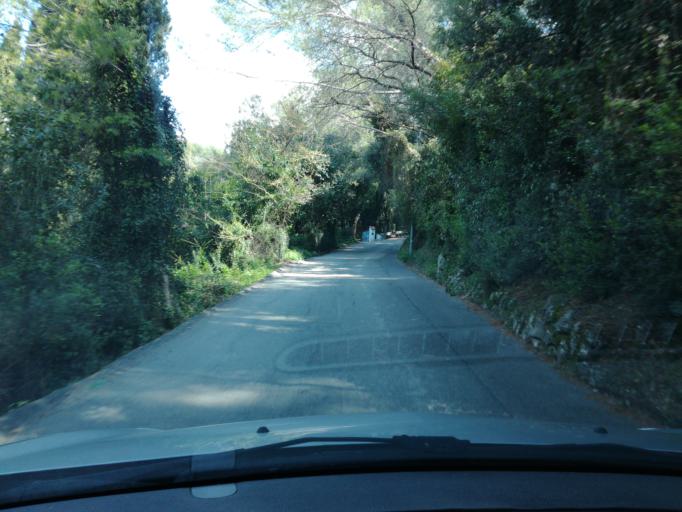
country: FR
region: Provence-Alpes-Cote d'Azur
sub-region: Departement des Alpes-Maritimes
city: Mougins
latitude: 43.6071
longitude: 6.9902
